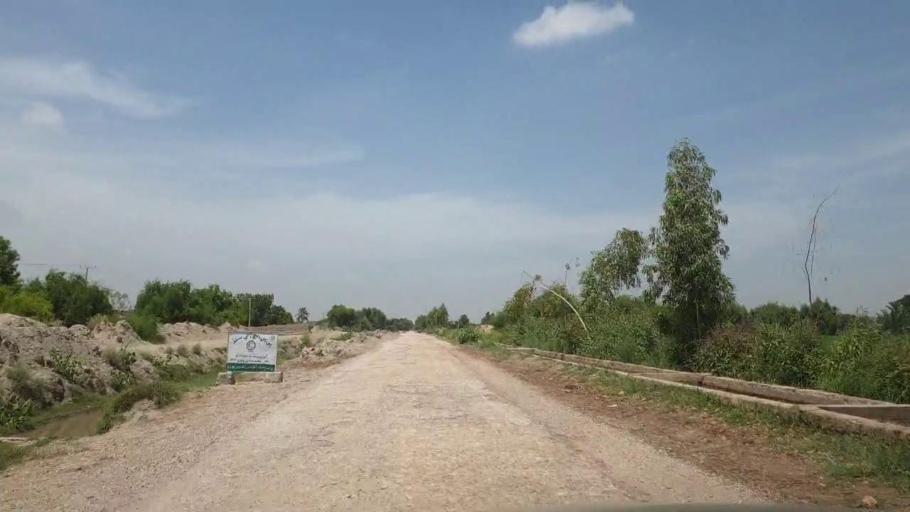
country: PK
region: Sindh
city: Kot Diji
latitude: 27.1354
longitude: 69.0359
